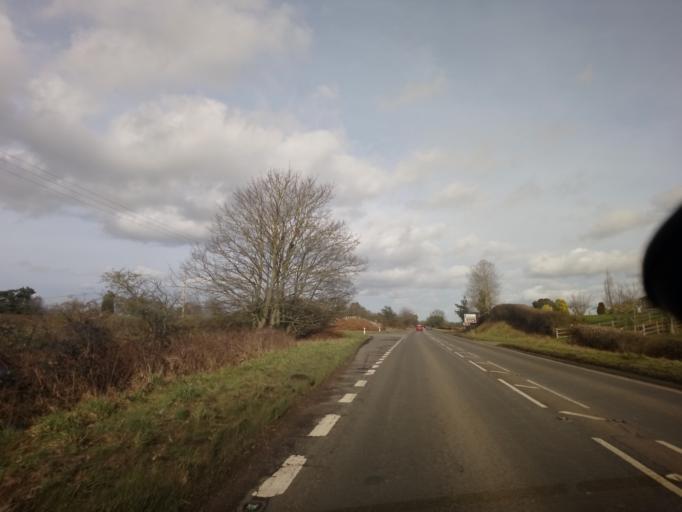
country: GB
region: England
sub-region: Shropshire
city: Stoke upon Tern
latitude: 52.7909
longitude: -2.5478
